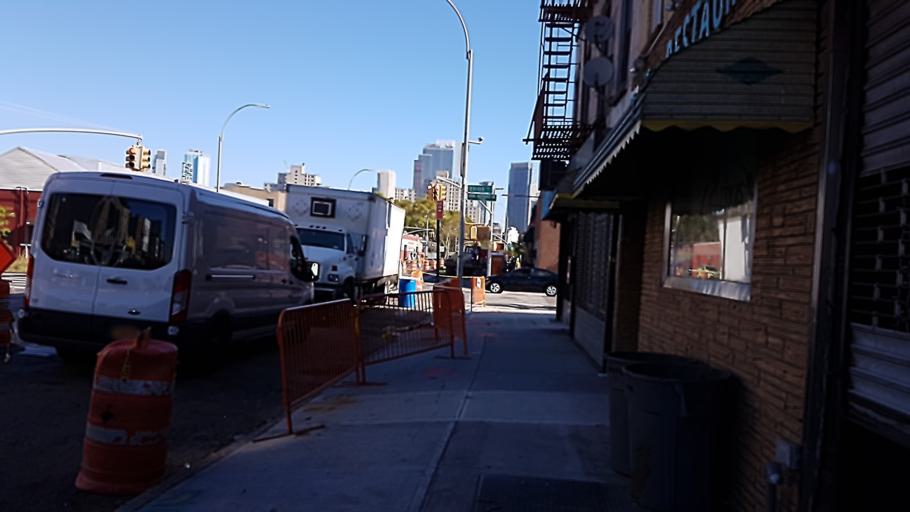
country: US
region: New York
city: New York City
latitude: 40.6781
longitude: -73.9855
